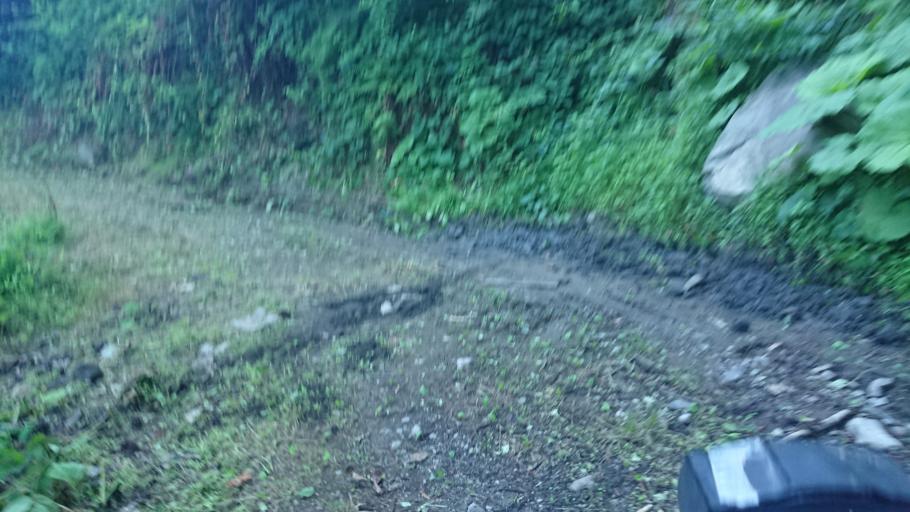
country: TR
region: Rize
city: Rize
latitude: 40.9733
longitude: 40.4966
